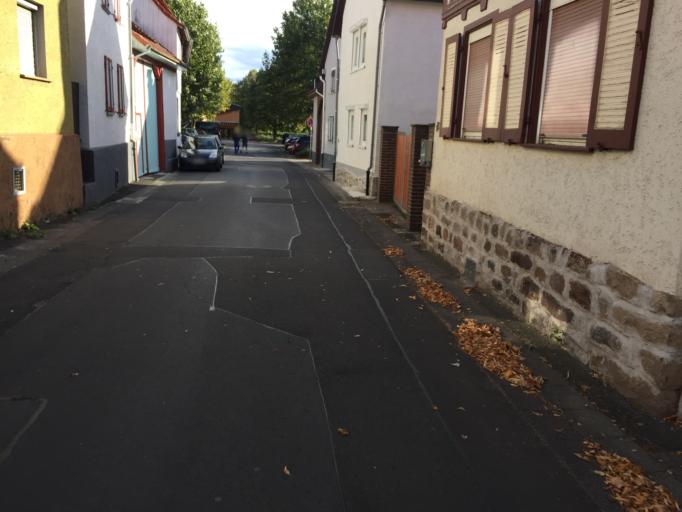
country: DE
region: Hesse
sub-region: Regierungsbezirk Darmstadt
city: Rockenberg
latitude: 50.4612
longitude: 8.7286
